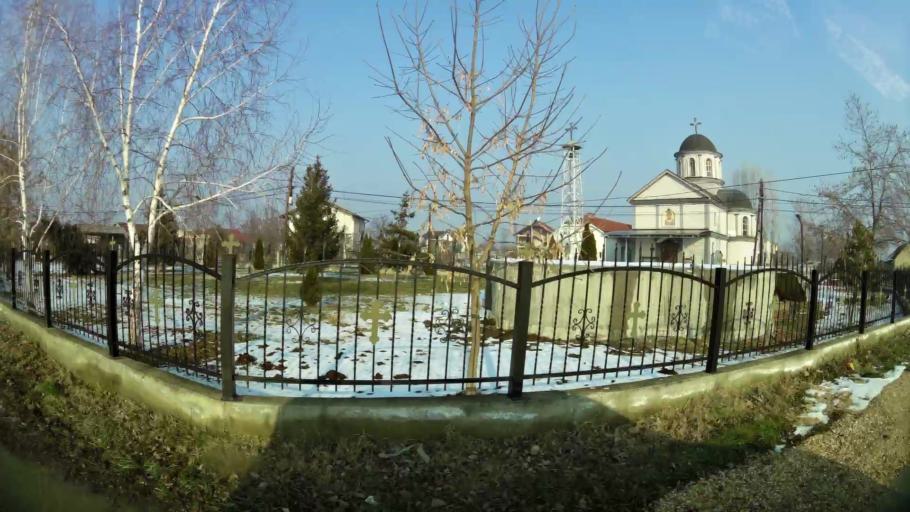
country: MK
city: Kadino
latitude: 41.9535
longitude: 21.6018
